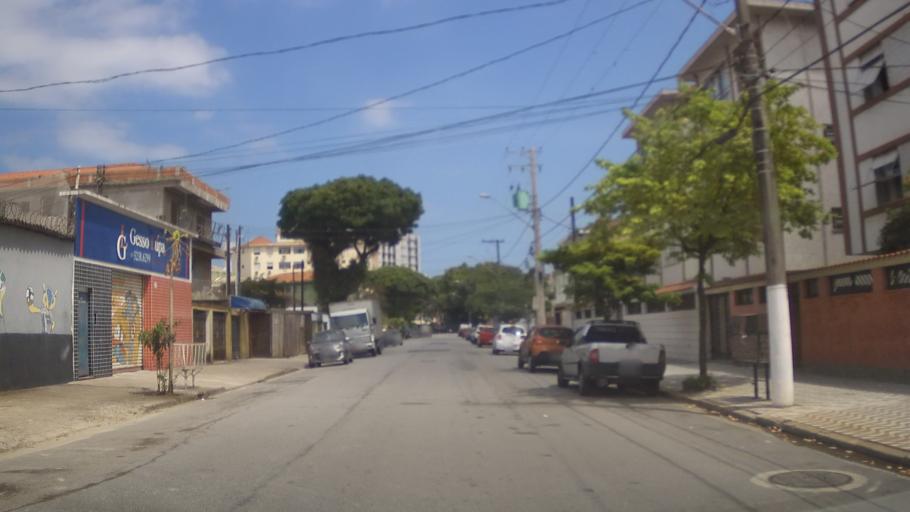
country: BR
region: Sao Paulo
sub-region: Santos
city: Santos
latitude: -23.9635
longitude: -46.3106
